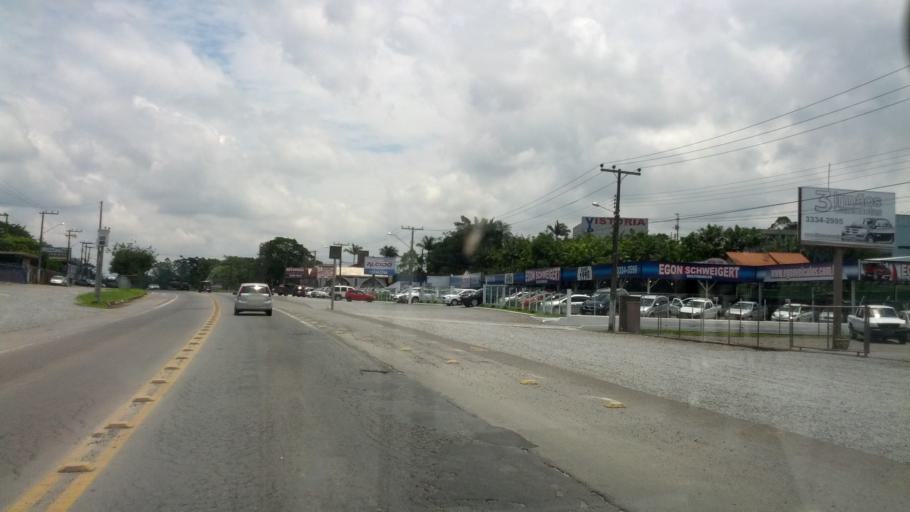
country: BR
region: Santa Catarina
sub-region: Blumenau
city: Blumenau
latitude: -26.8767
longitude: -49.1274
